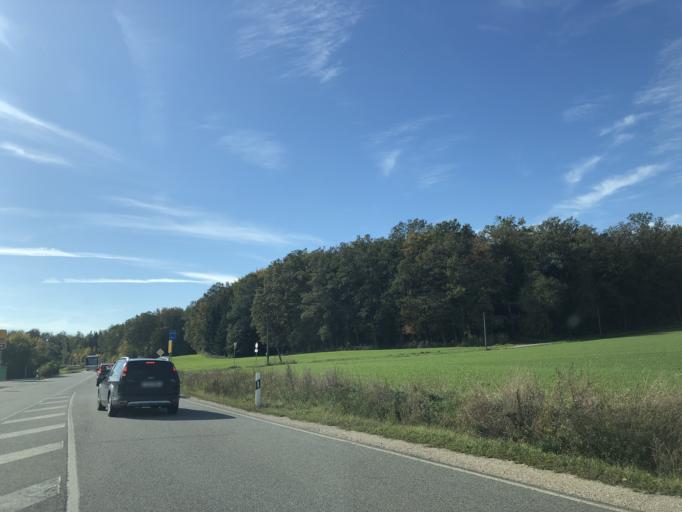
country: DE
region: Bavaria
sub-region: Upper Palatinate
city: Brunn
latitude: 49.0895
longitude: 11.8865
